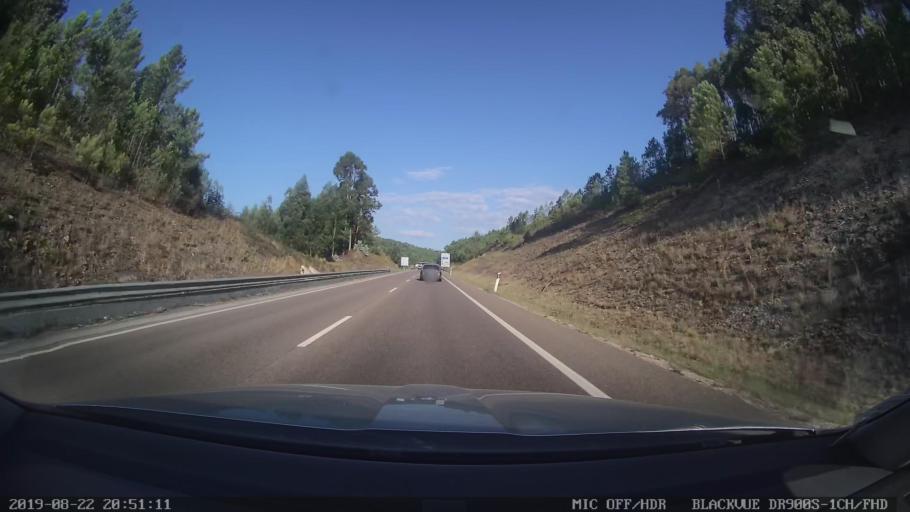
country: PT
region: Castelo Branco
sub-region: Proenca-A-Nova
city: Proenca-a-Nova
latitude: 39.7588
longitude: -7.9543
